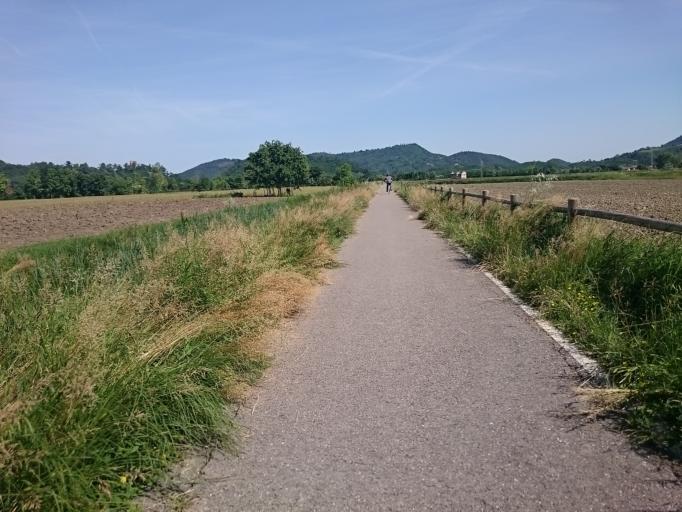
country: IT
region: Veneto
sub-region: Provincia di Padova
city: Montemerlo
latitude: 45.3750
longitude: 11.6915
